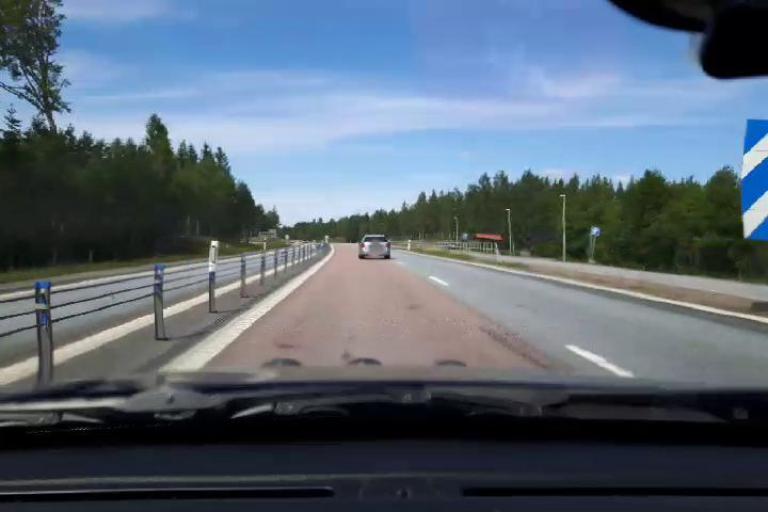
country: SE
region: Gaevleborg
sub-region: Gavle Kommun
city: Gavle
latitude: 60.7941
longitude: 17.0828
